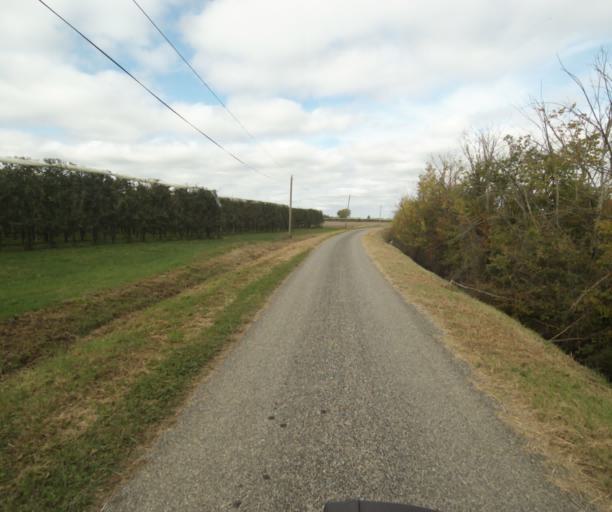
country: FR
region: Midi-Pyrenees
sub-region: Departement du Tarn-et-Garonne
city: Finhan
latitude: 43.9286
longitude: 1.2060
